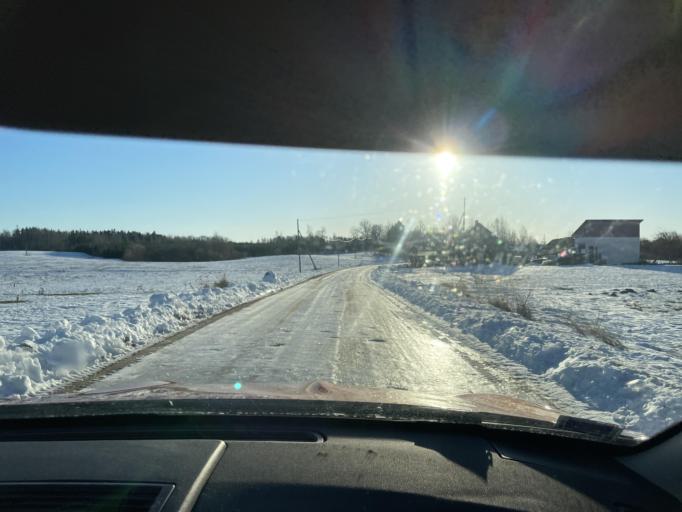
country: LV
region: Ludzas Rajons
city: Ludza
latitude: 56.4694
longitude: 27.6013
